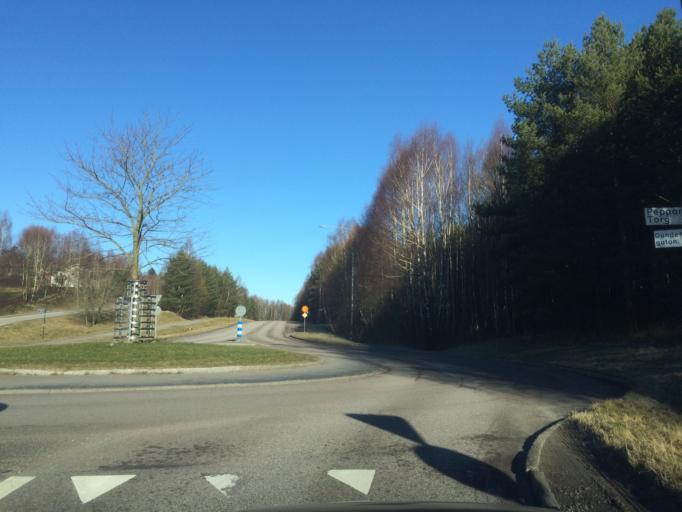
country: SE
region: Vaestra Goetaland
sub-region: Molndal
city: Moelndal
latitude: 57.6311
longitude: 12.0242
